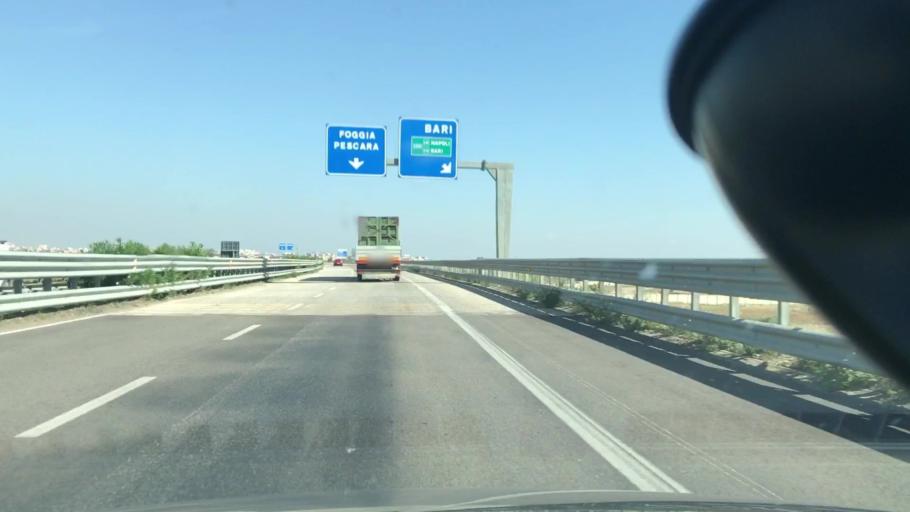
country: IT
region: Apulia
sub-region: Provincia di Foggia
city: Foggia
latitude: 41.4220
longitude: 15.5591
